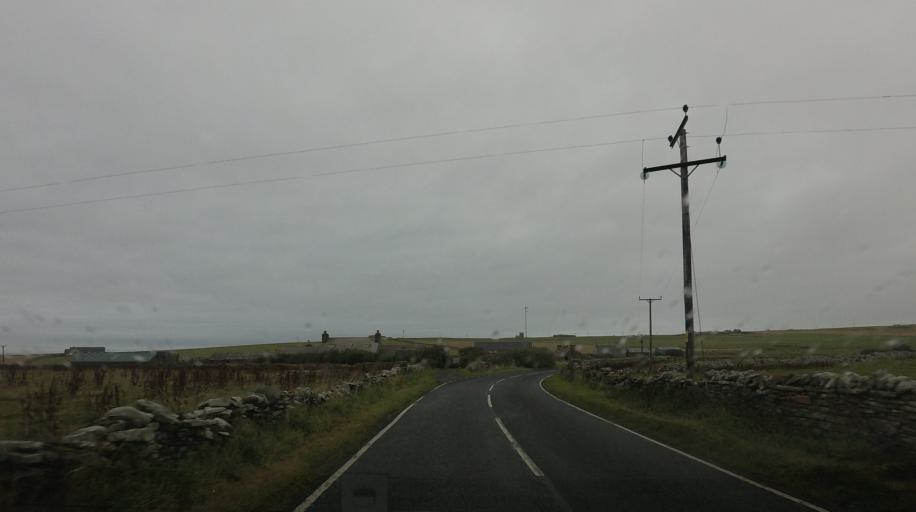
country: GB
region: Scotland
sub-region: Orkney Islands
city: Stromness
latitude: 59.1261
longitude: -3.3042
